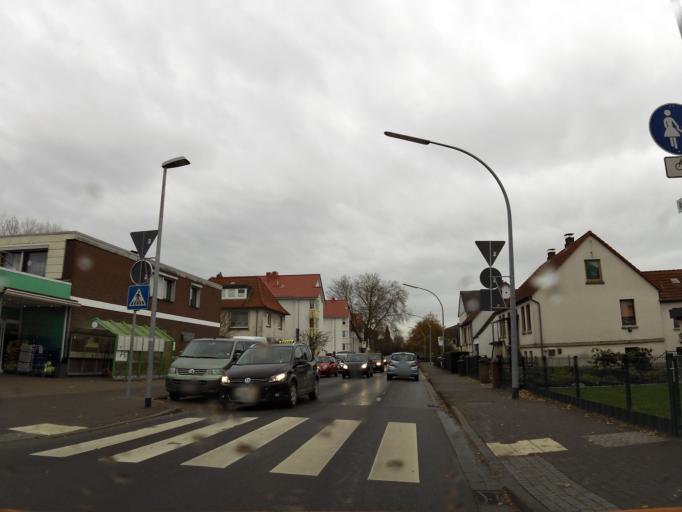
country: DE
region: Lower Saxony
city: Oldenburg
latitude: 53.1148
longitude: 8.2162
